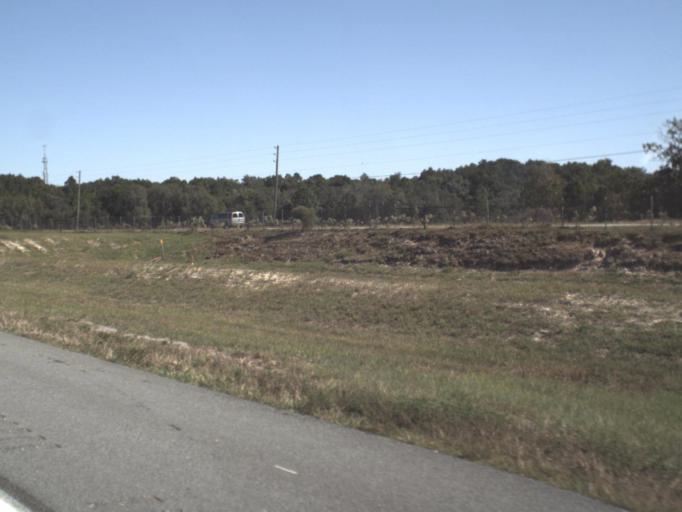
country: US
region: Florida
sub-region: Pasco County
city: Shady Hills
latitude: 28.3797
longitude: -82.5404
